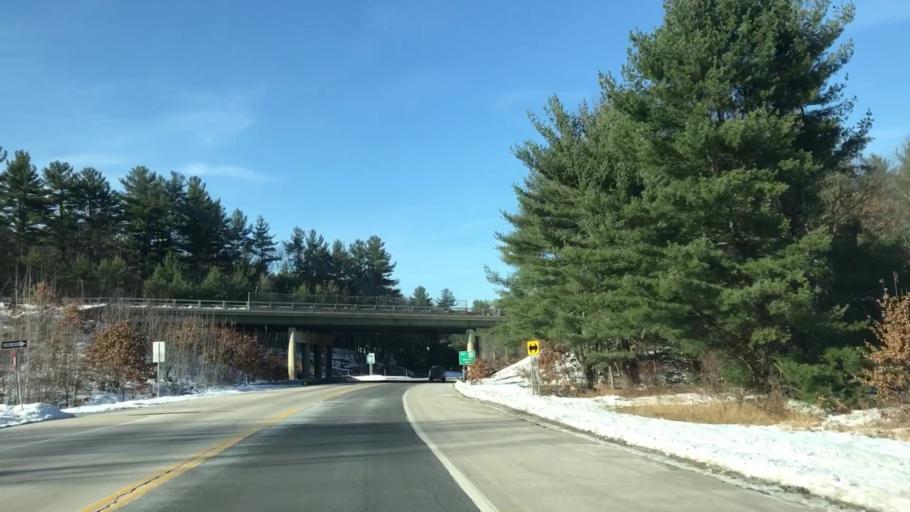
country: US
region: New Hampshire
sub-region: Hillsborough County
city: Milford
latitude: 42.8446
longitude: -71.6149
